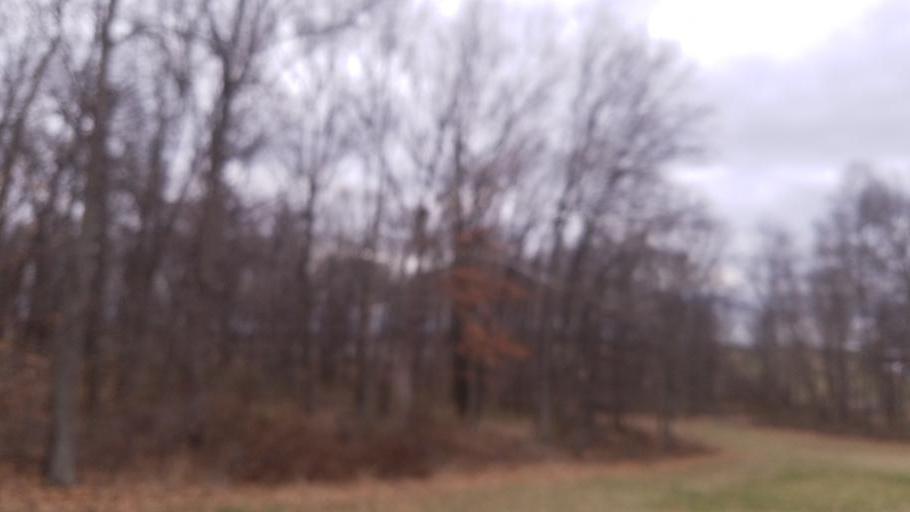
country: US
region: Ohio
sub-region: Licking County
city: Utica
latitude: 40.2221
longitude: -82.4004
